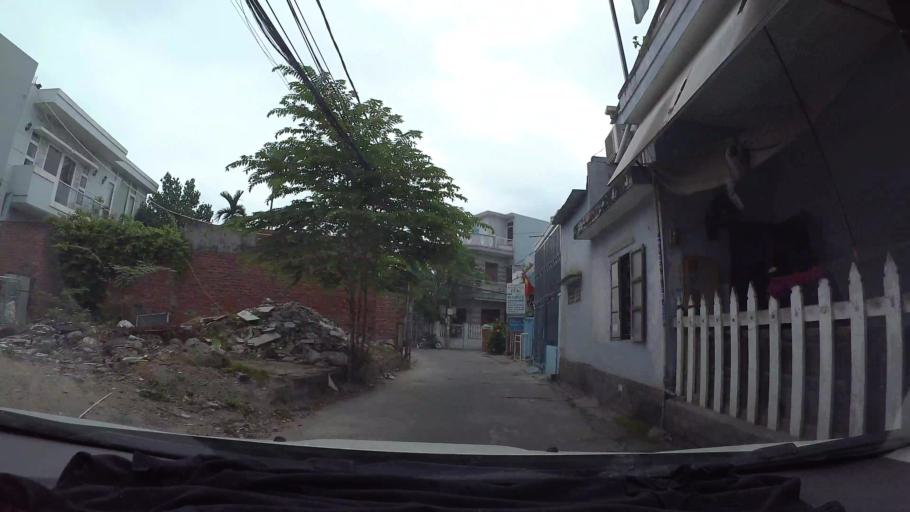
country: VN
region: Da Nang
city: Lien Chieu
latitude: 16.0588
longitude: 108.1685
